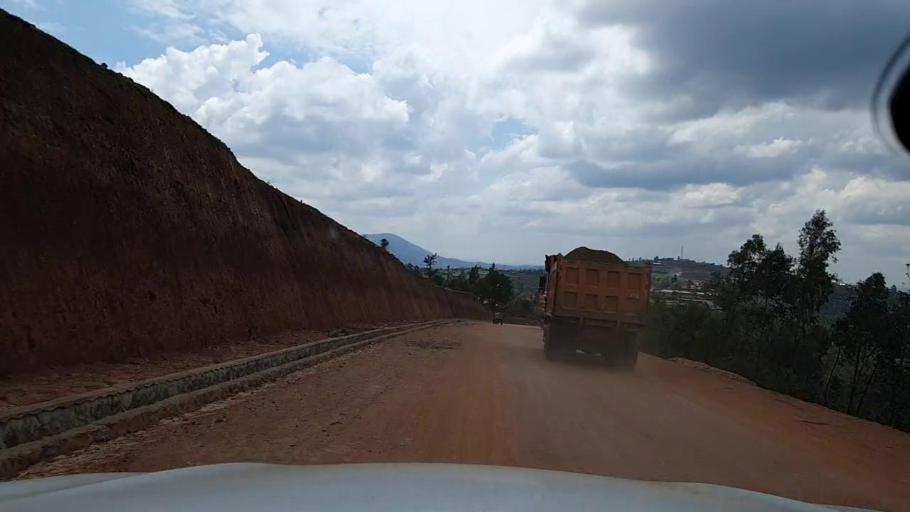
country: RW
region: Southern Province
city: Butare
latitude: -2.6879
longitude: 29.5651
